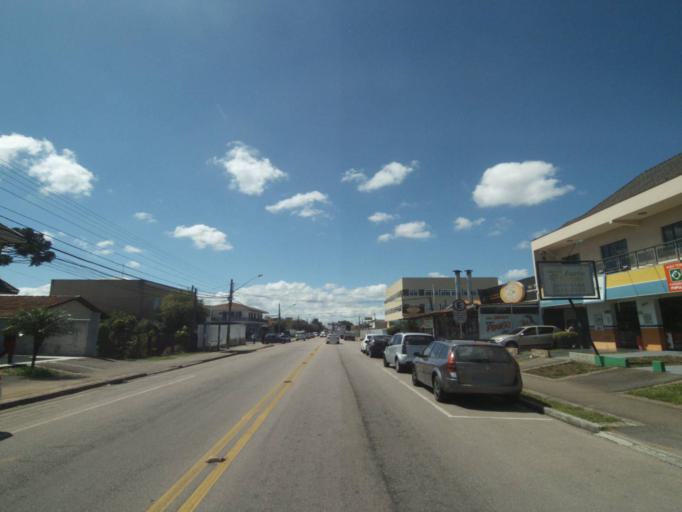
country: BR
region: Parana
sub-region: Pinhais
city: Pinhais
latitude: -25.4424
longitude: -49.2106
